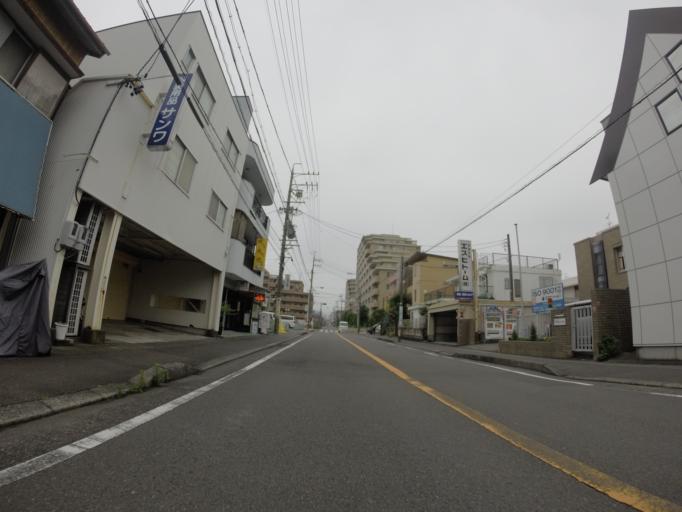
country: JP
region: Shizuoka
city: Shizuoka-shi
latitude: 34.9623
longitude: 138.3965
